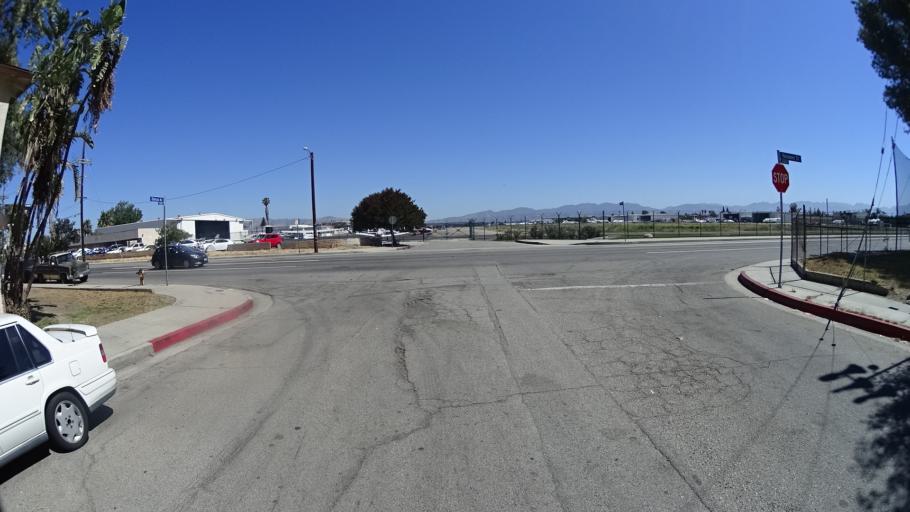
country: US
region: California
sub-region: Los Angeles County
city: Van Nuys
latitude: 34.1936
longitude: -118.4900
